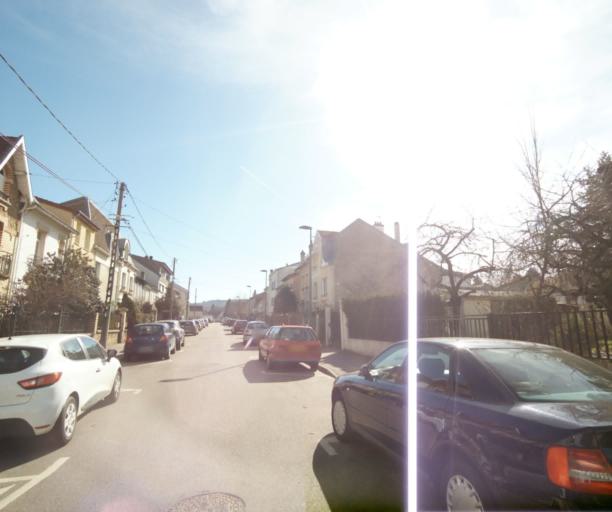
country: FR
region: Lorraine
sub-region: Departement de Meurthe-et-Moselle
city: Villers-les-Nancy
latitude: 48.6737
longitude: 6.1499
